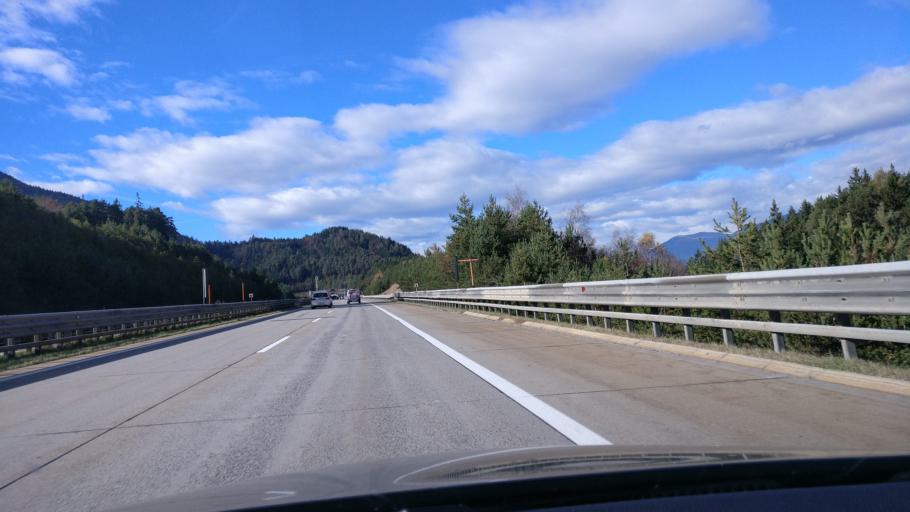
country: AT
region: Carinthia
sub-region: Politischer Bezirk Villach Land
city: Fresach
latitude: 46.6576
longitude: 13.7331
